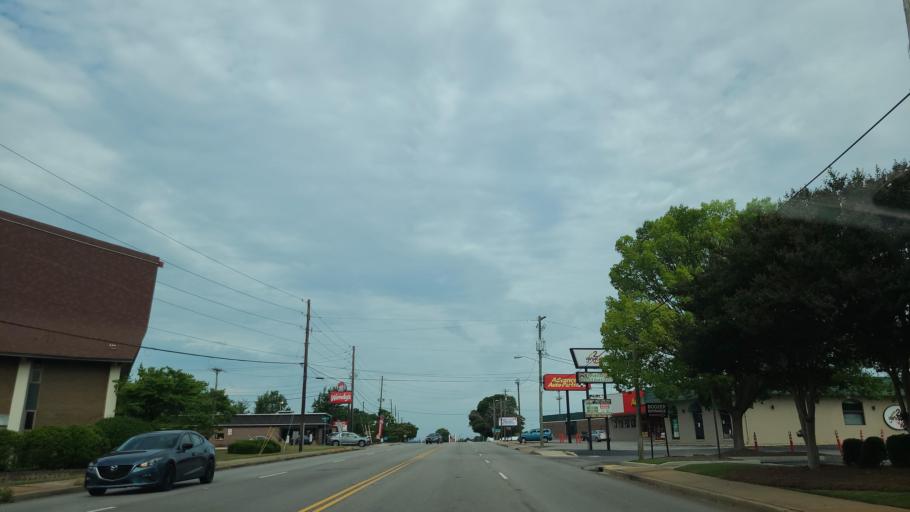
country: US
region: South Carolina
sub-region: Lexington County
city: West Columbia
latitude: 34.0308
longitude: -81.0888
